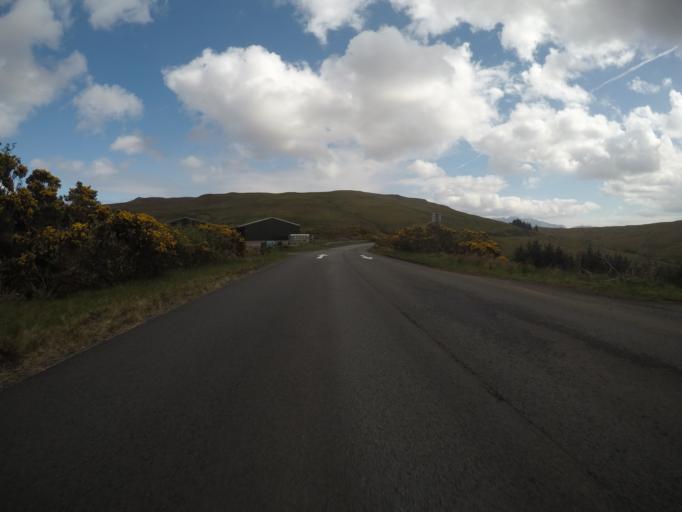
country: GB
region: Scotland
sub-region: Highland
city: Isle of Skye
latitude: 57.3292
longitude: -6.3354
